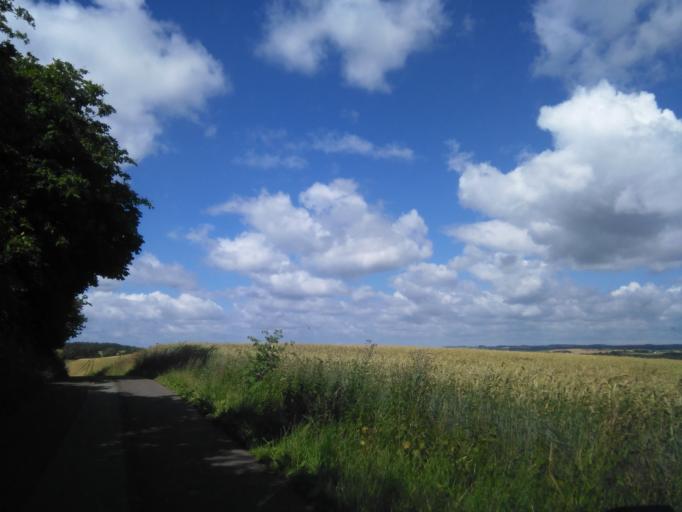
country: DK
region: Central Jutland
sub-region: Syddjurs Kommune
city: Ronde
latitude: 56.1735
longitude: 10.4209
